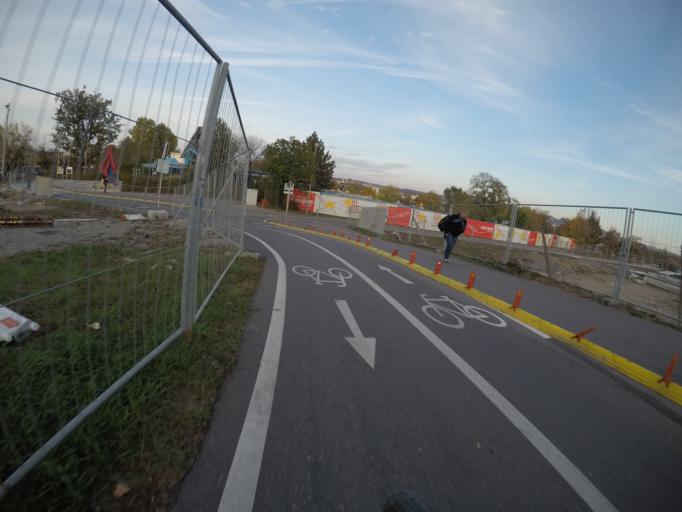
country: DE
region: Baden-Wuerttemberg
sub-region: Regierungsbezirk Stuttgart
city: Stuttgart-Ost
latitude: 48.7982
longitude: 9.2097
